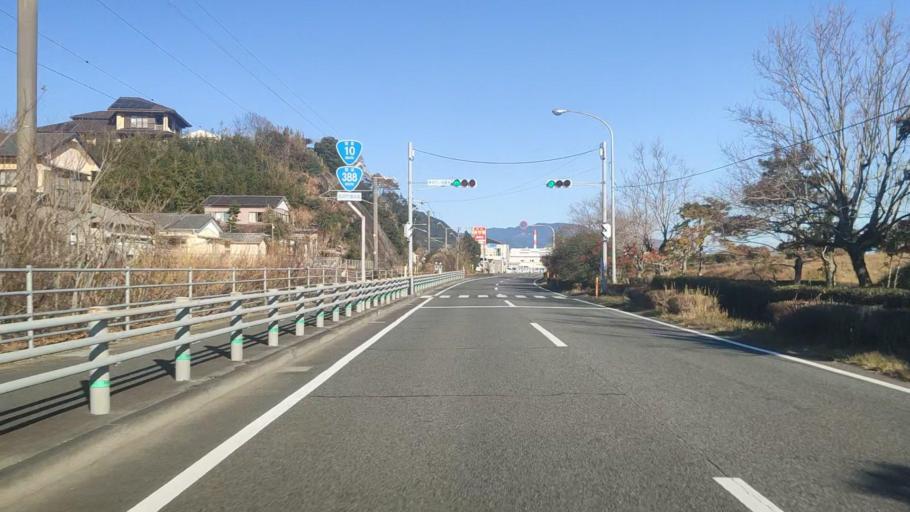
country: JP
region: Miyazaki
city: Nobeoka
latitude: 32.5392
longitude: 131.6787
